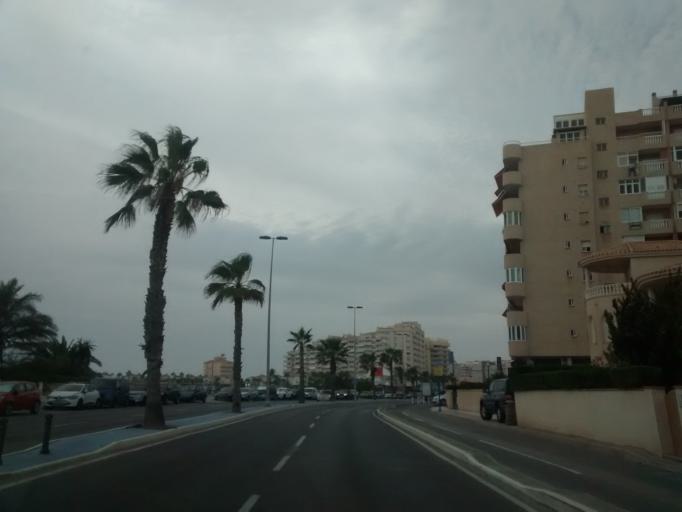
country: ES
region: Murcia
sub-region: Murcia
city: La Manga del Mar Menor
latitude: 37.7039
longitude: -0.7414
